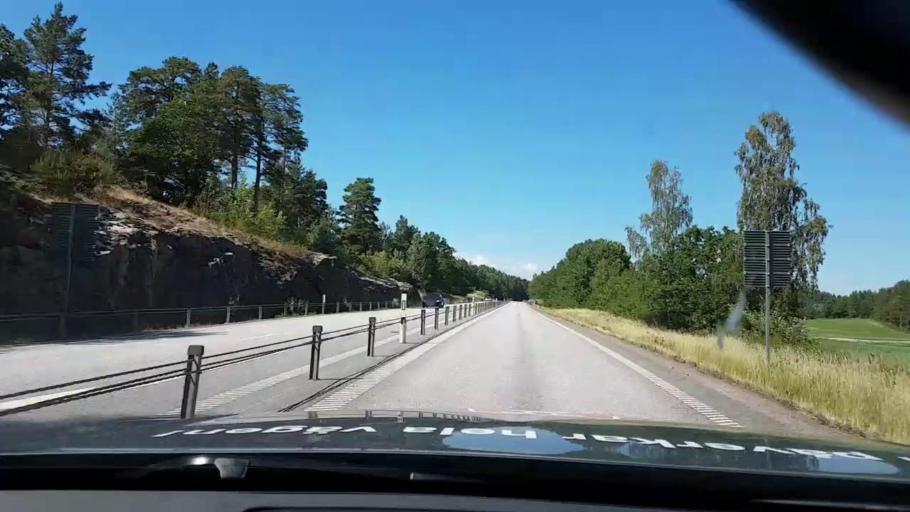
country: SE
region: Kalmar
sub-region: Vasterviks Kommun
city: Gamleby
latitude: 57.9211
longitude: 16.3995
